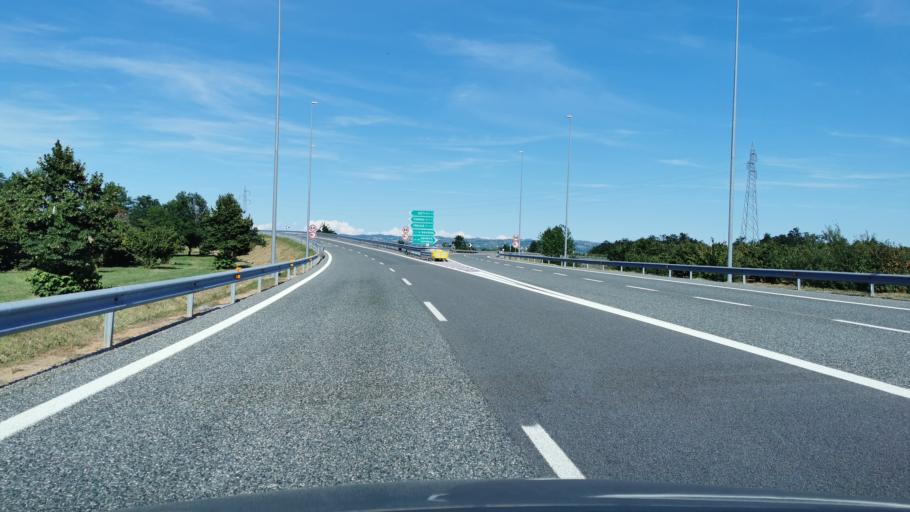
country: IT
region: Piedmont
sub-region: Provincia di Cuneo
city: Magliano Alpi
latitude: 44.4854
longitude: 7.8158
